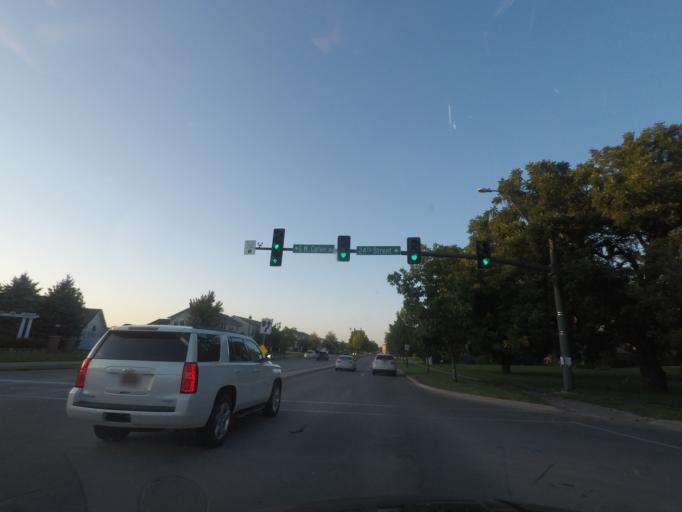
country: US
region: Iowa
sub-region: Story County
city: Ames
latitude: 42.0455
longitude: -93.6448
